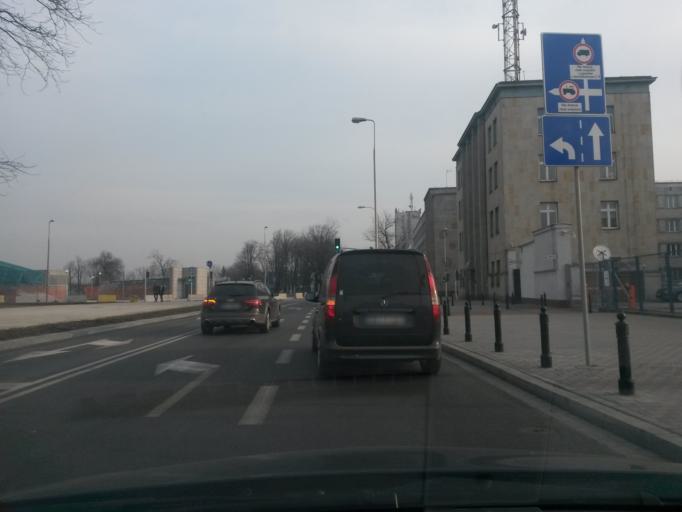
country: PL
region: Masovian Voivodeship
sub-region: Warszawa
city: Praga Polnoc
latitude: 52.2400
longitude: 21.0299
